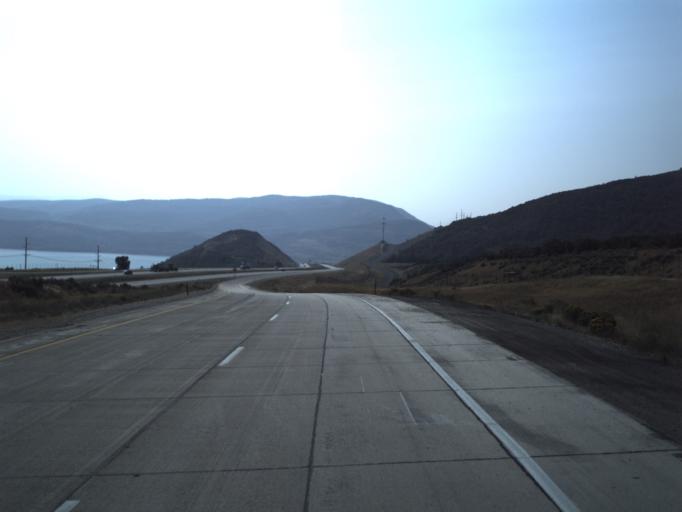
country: US
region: Utah
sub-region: Summit County
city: Park City
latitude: 40.6246
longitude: -111.4414
